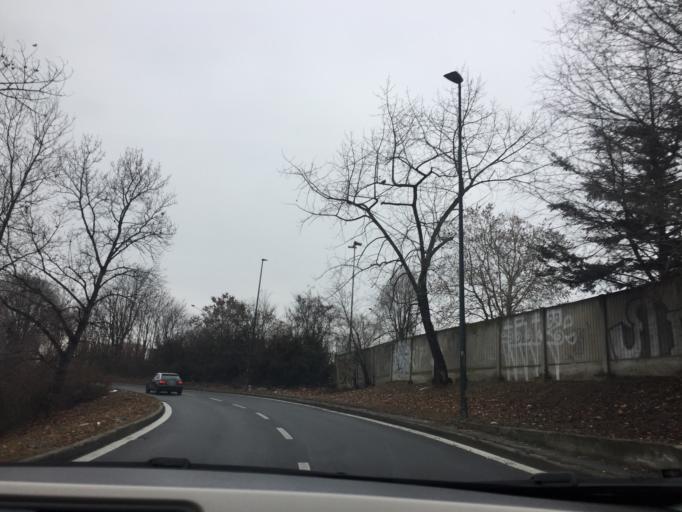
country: IT
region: Piedmont
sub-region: Provincia di Torino
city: Savonera
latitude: 45.0981
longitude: 7.6239
